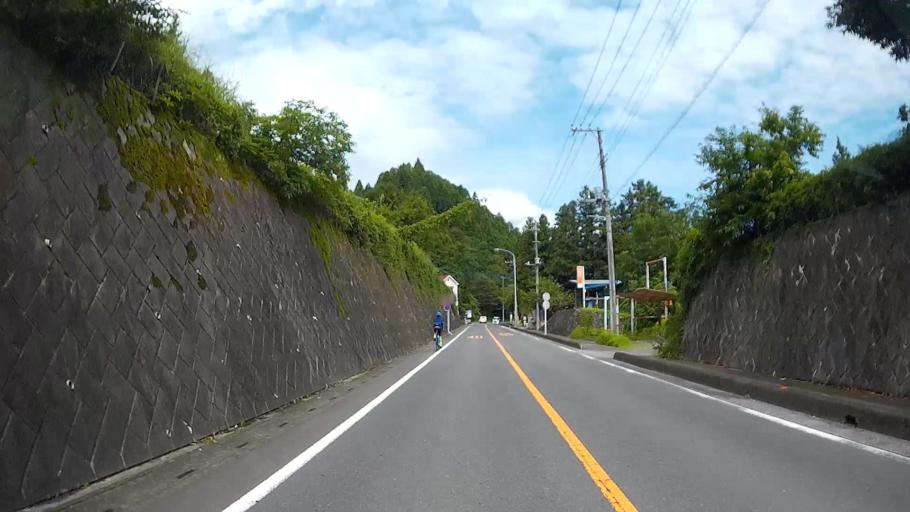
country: JP
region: Tokyo
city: Ome
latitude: 35.8551
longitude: 139.1929
